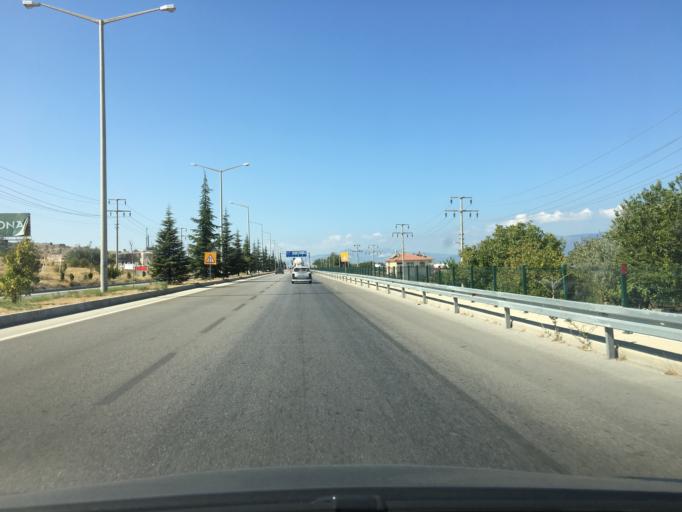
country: TR
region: Burdur
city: Burdur
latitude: 37.7500
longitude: 30.3276
